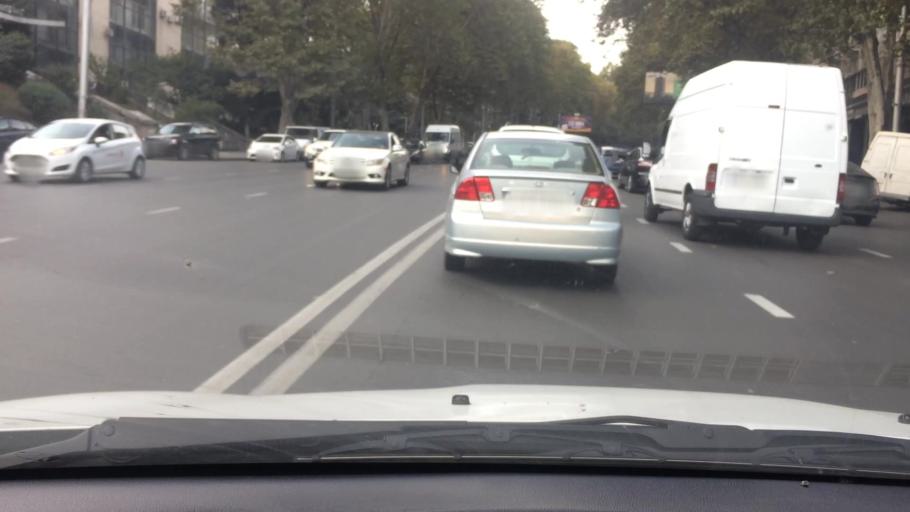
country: GE
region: T'bilisi
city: Tbilisi
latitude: 41.7143
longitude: 44.7800
